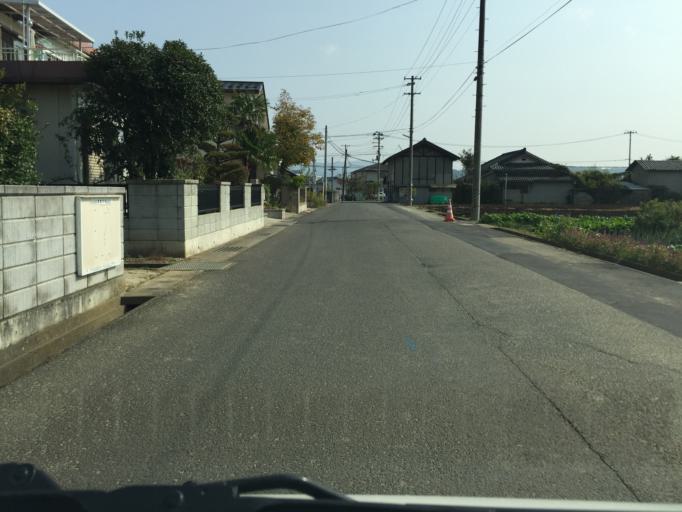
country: JP
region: Fukushima
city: Fukushima-shi
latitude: 37.7238
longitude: 140.4370
